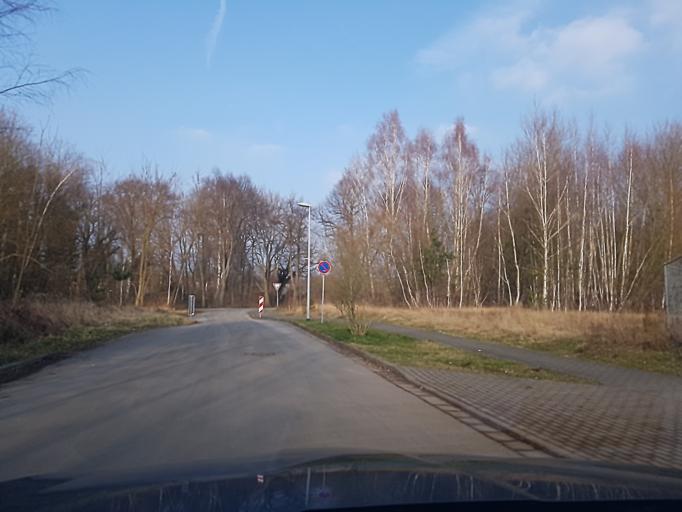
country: DE
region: Brandenburg
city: Finsterwalde
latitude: 51.6285
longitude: 13.6968
